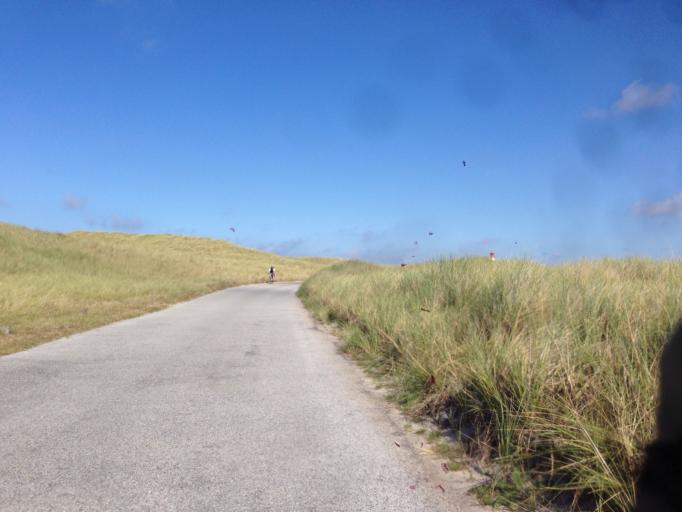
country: DE
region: Schleswig-Holstein
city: List
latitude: 55.0503
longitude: 8.3976
